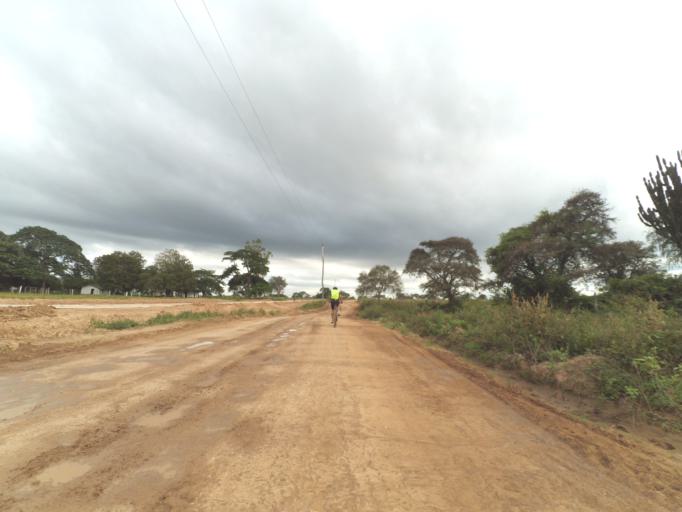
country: BO
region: Santa Cruz
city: Santa Cruz de la Sierra
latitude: -17.7132
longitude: -63.2757
